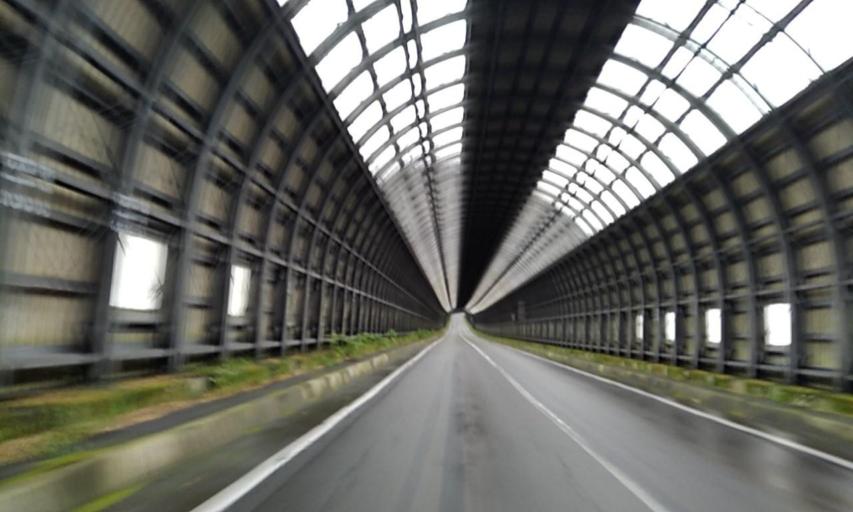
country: JP
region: Hokkaido
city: Abashiri
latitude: 43.6129
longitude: 144.5931
